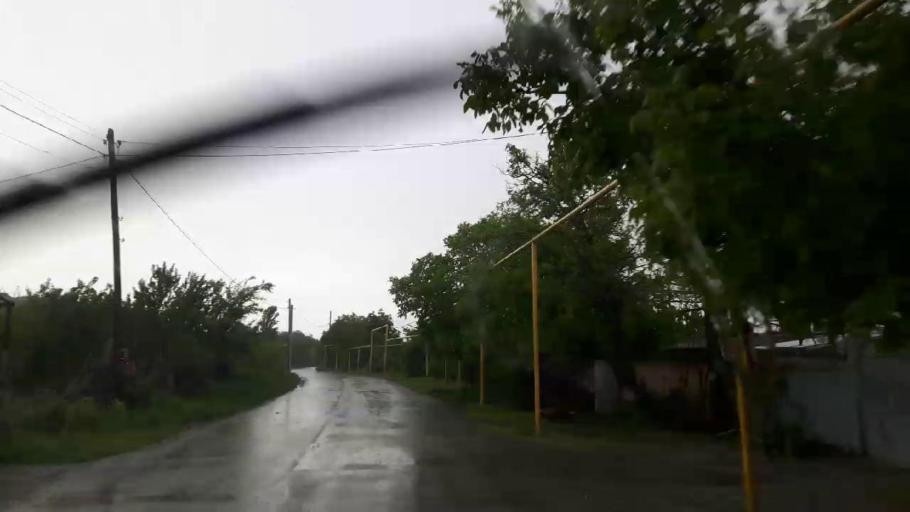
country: GE
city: Agara
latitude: 42.0147
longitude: 43.8482
